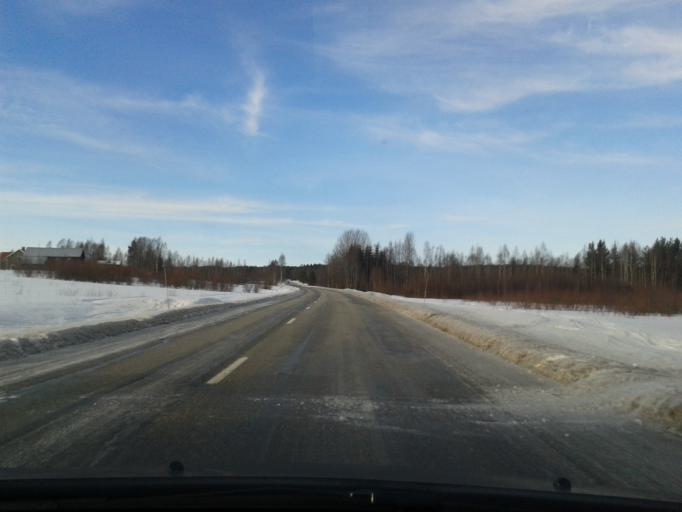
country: SE
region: Vaesternorrland
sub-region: OErnskoeldsviks Kommun
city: Bredbyn
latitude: 63.5689
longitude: 17.9304
